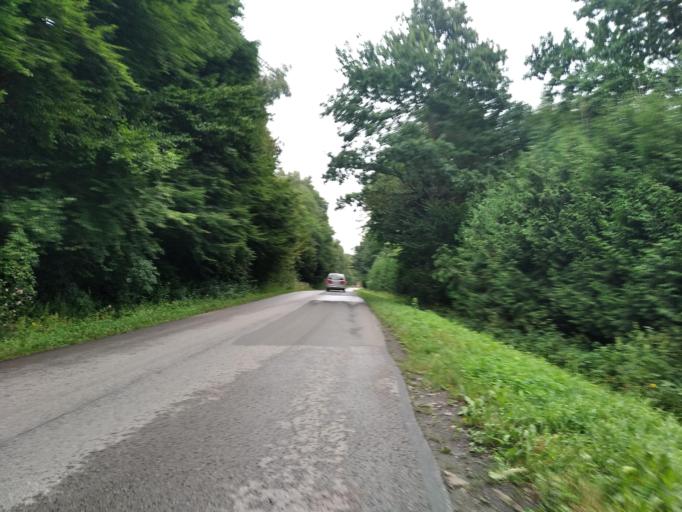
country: PL
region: Subcarpathian Voivodeship
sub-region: Powiat brzozowski
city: Nozdrzec
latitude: 49.7239
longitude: 22.2952
